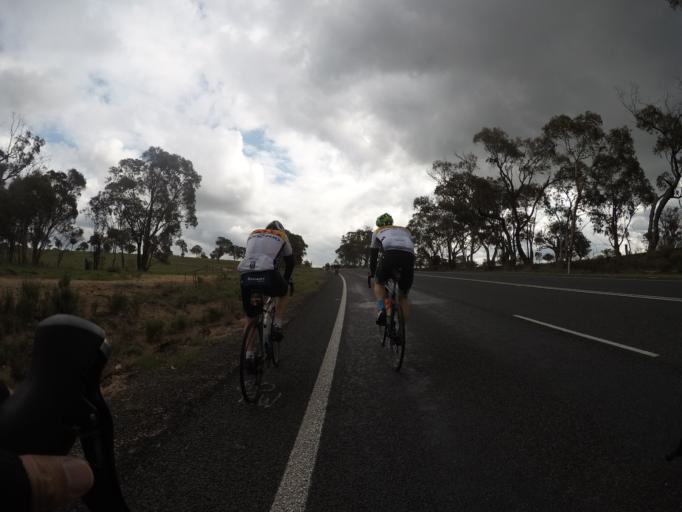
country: AU
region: New South Wales
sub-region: Bathurst Regional
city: Eglinton
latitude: -33.4238
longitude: 149.4002
